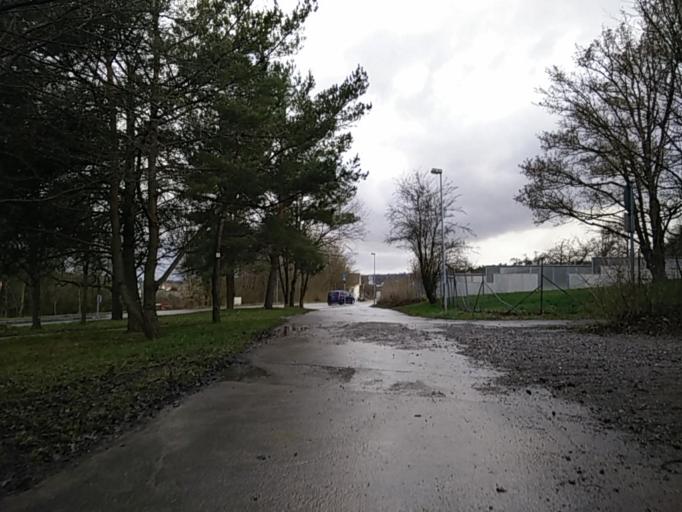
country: DE
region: Baden-Wuerttemberg
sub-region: Tuebingen Region
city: Tuebingen
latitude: 48.5387
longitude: 9.0303
